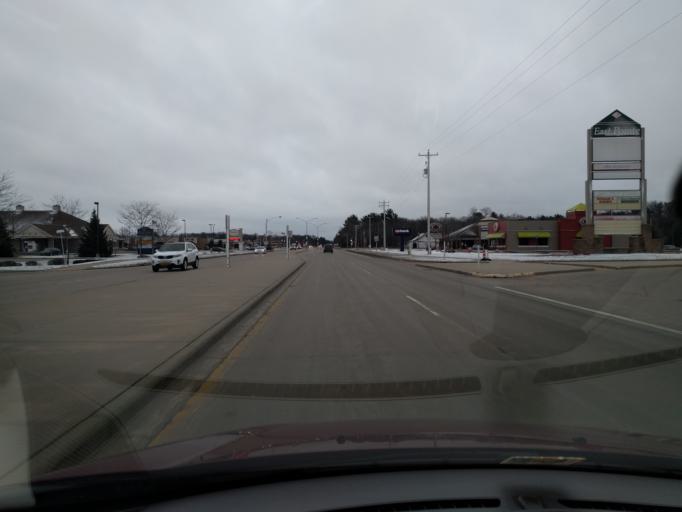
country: US
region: Wisconsin
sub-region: Portage County
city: Whiting
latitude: 44.5234
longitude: -89.5064
